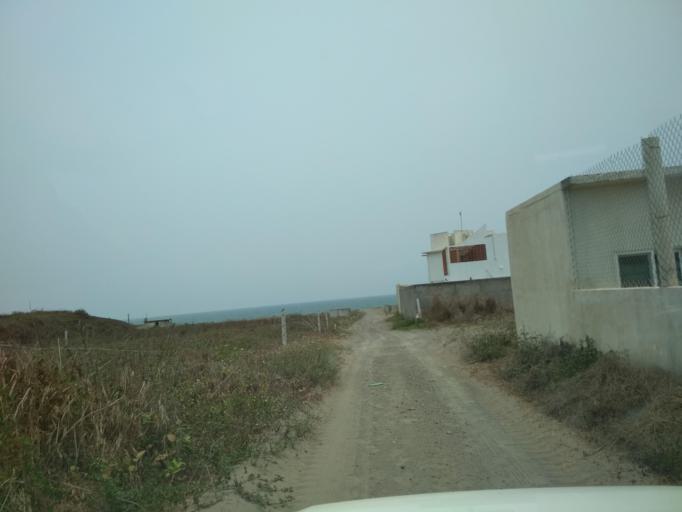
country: MX
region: Veracruz
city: Anton Lizardo
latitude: 19.0566
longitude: -96.0426
